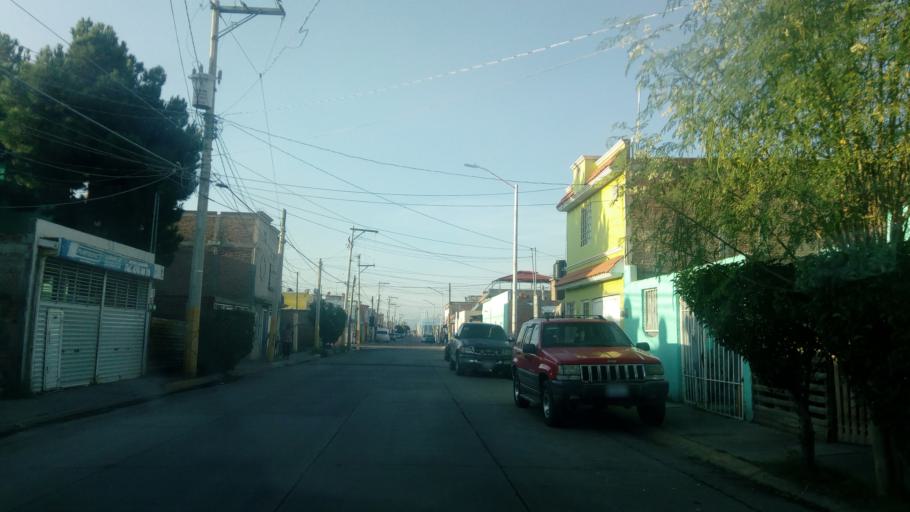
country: MX
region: Durango
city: Victoria de Durango
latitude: 24.0696
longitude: -104.5892
